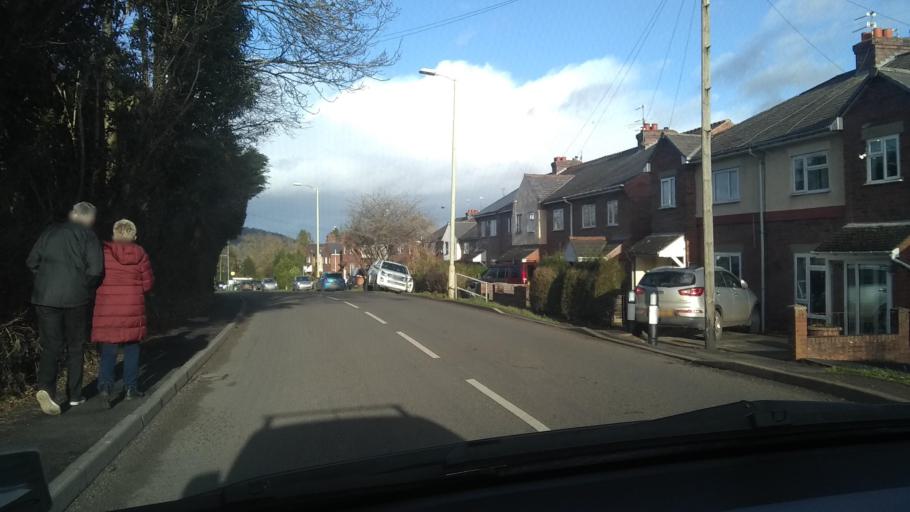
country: GB
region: England
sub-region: Worcestershire
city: Bewdley
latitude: 52.3735
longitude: -2.3328
